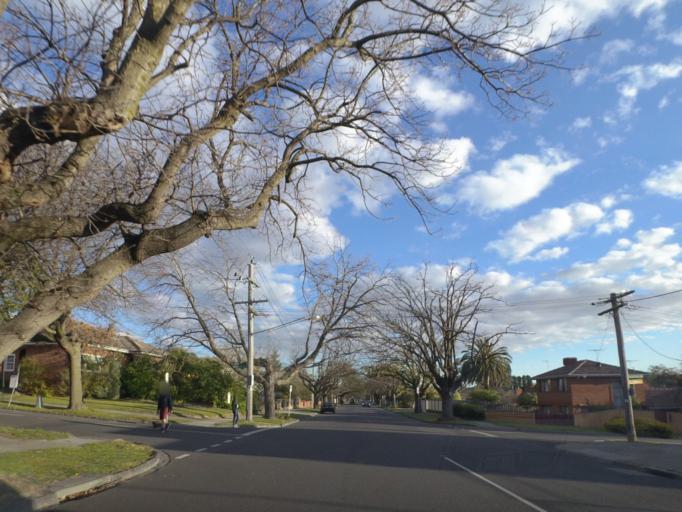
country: AU
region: Victoria
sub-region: Whitehorse
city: Surrey Hills
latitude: -37.8363
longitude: 145.0933
